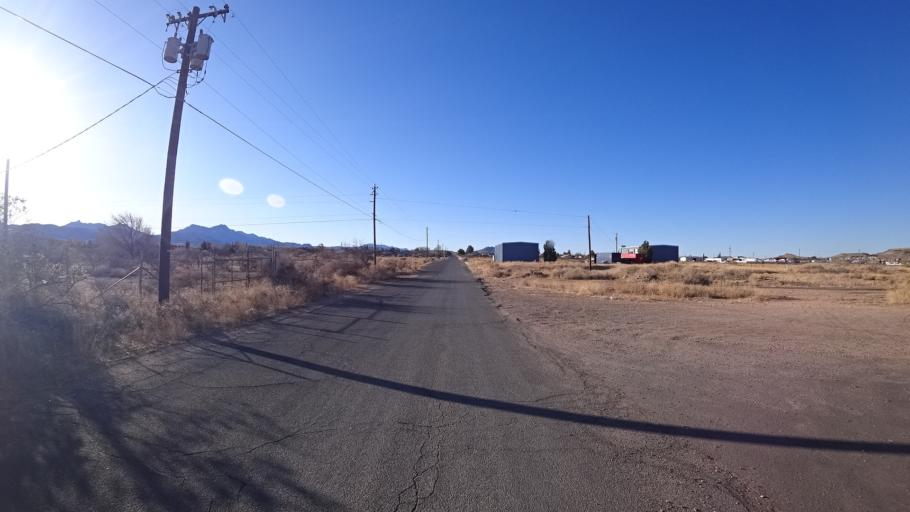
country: US
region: Arizona
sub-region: Mohave County
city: Kingman
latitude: 35.2094
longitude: -114.0137
